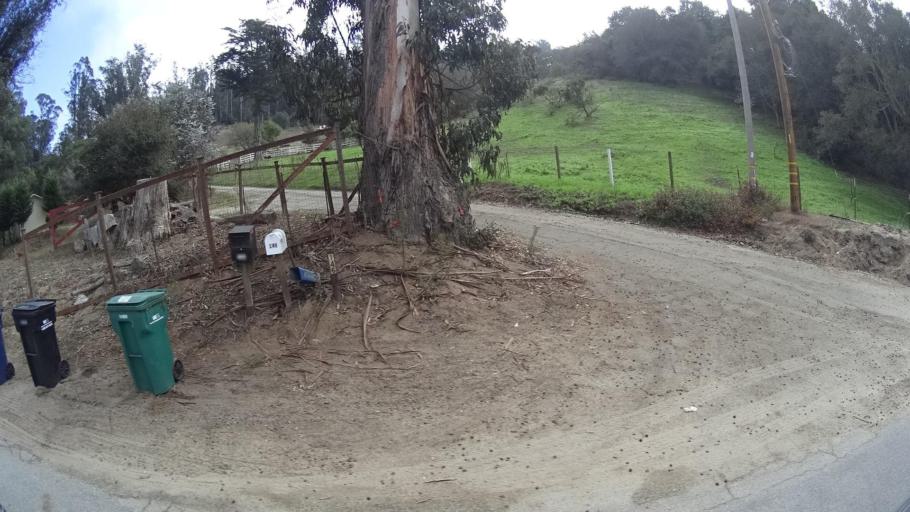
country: US
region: California
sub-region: Monterey County
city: Las Lomas
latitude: 36.8893
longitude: -121.7191
